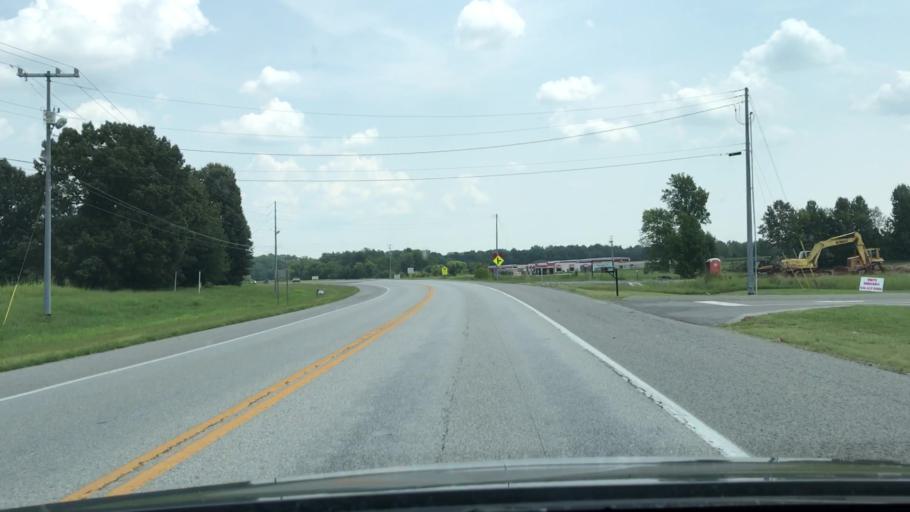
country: US
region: Tennessee
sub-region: Sumner County
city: Portland
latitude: 36.5800
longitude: -86.5609
